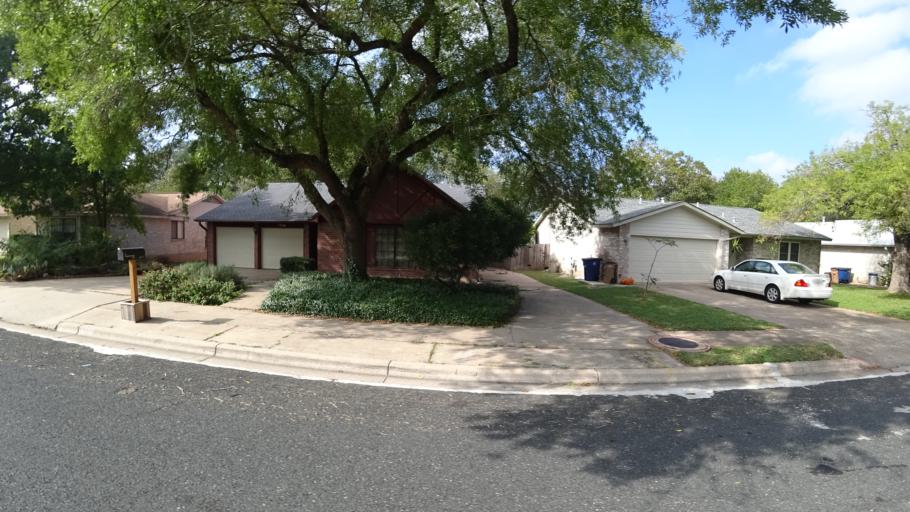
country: US
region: Texas
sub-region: Travis County
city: Shady Hollow
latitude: 30.2000
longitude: -97.8188
